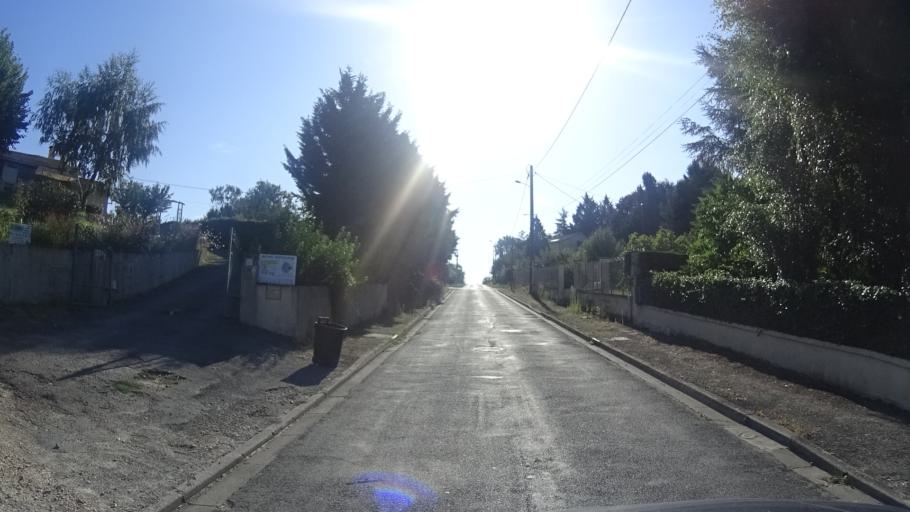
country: FR
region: Aquitaine
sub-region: Departement de la Dordogne
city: Mussidan
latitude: 45.0335
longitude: 0.3745
